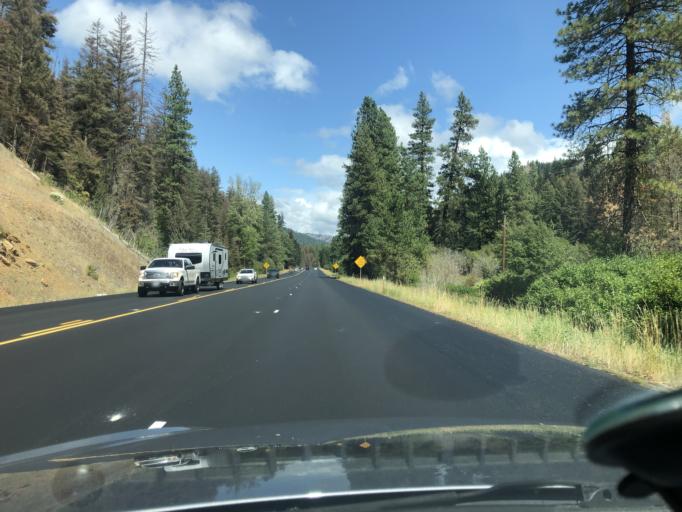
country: US
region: Washington
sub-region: Kittitas County
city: Cle Elum
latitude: 47.2686
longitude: -120.6977
